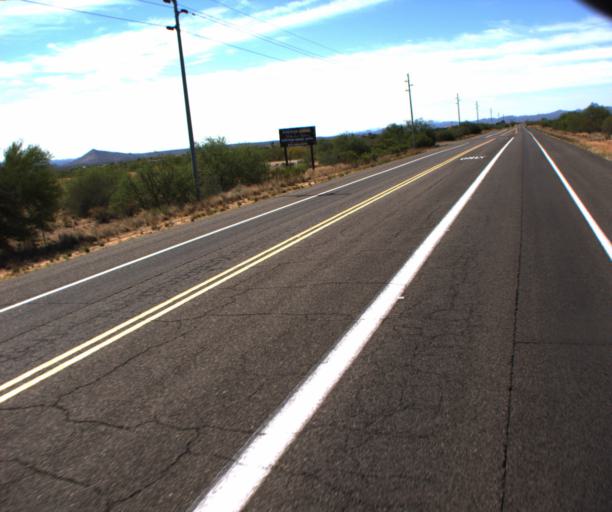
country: US
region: Arizona
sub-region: Yavapai County
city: Congress
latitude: 34.1127
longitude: -112.8338
